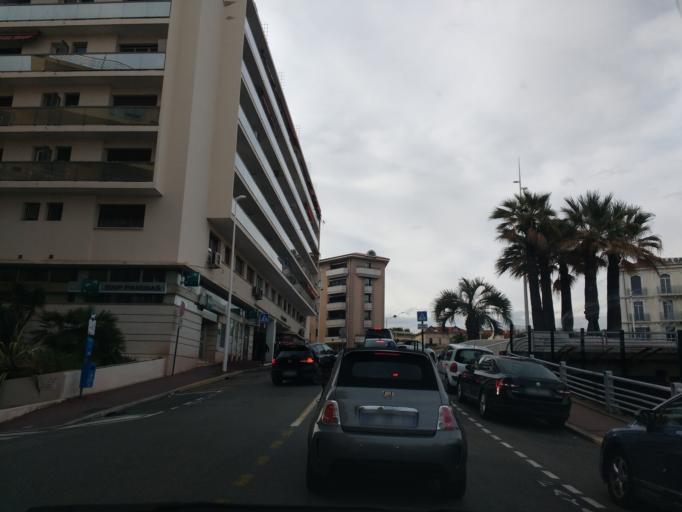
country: FR
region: Provence-Alpes-Cote d'Azur
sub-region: Departement des Alpes-Maritimes
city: Cannes
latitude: 43.5505
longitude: 7.0303
